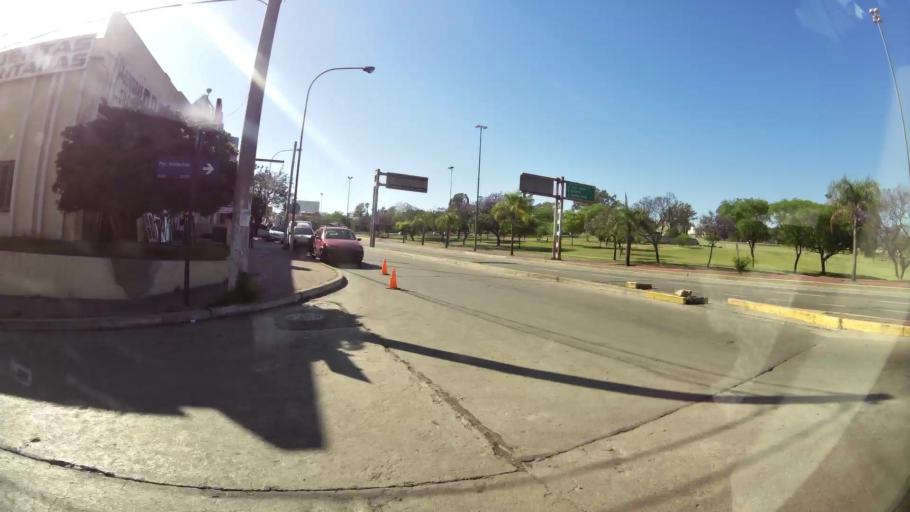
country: AR
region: Cordoba
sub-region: Departamento de Capital
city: Cordoba
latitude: -31.4299
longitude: -64.1690
